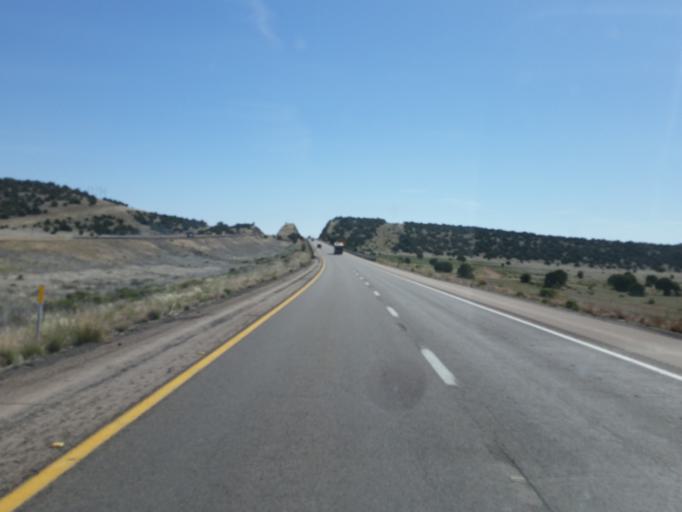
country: US
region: Arizona
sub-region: Mohave County
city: Peach Springs
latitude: 35.2346
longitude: -113.2108
